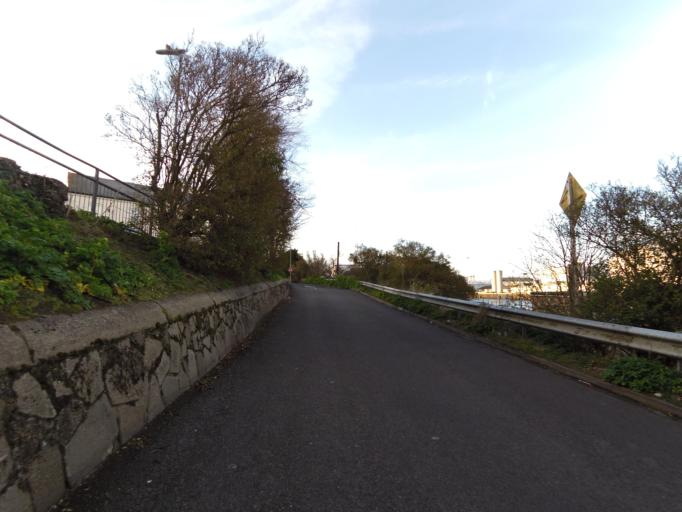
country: GB
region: England
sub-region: Norfolk
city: Gorleston-on-Sea
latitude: 52.5880
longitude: 1.7280
